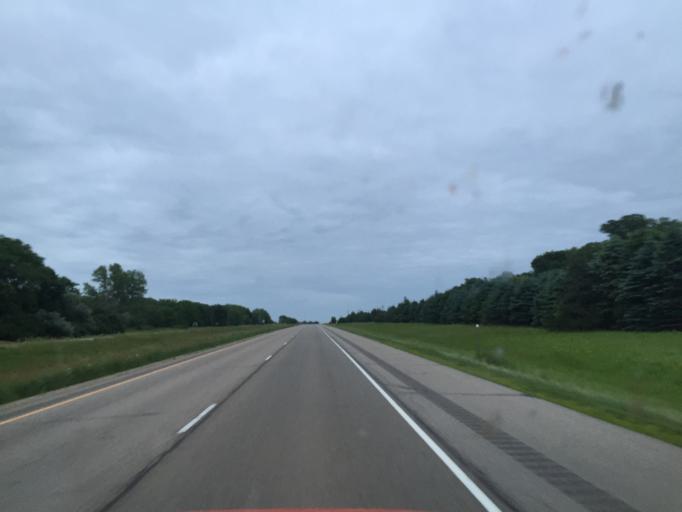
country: US
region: Minnesota
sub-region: Mower County
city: Austin
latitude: 43.6596
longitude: -93.1152
